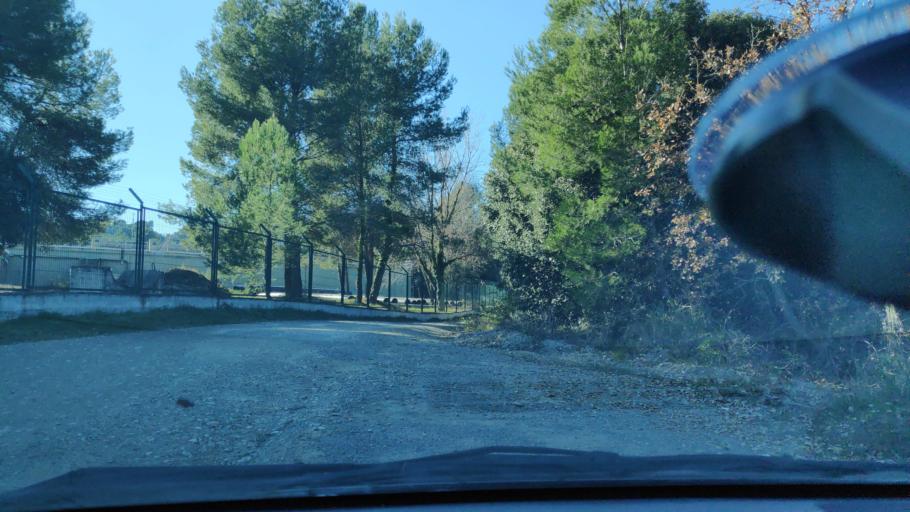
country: ES
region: Catalonia
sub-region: Provincia de Barcelona
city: Sant Quirze del Valles
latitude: 41.5364
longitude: 2.0538
